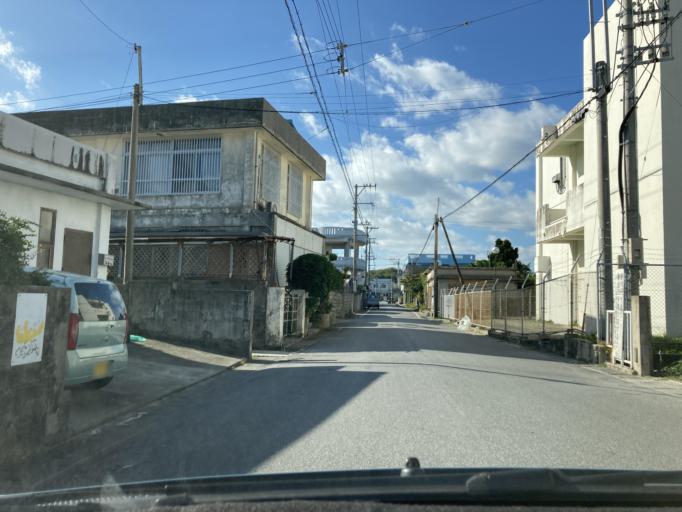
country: JP
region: Okinawa
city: Katsuren-haebaru
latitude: 26.3217
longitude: 127.9125
